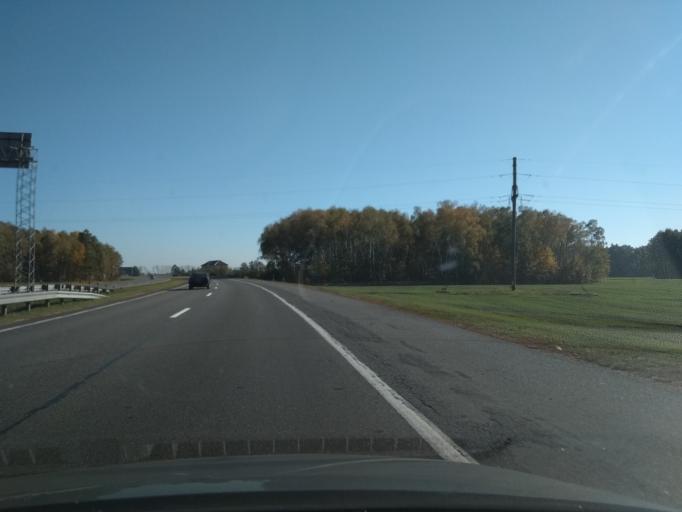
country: BY
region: Brest
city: Kobryn
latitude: 52.1783
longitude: 24.3384
